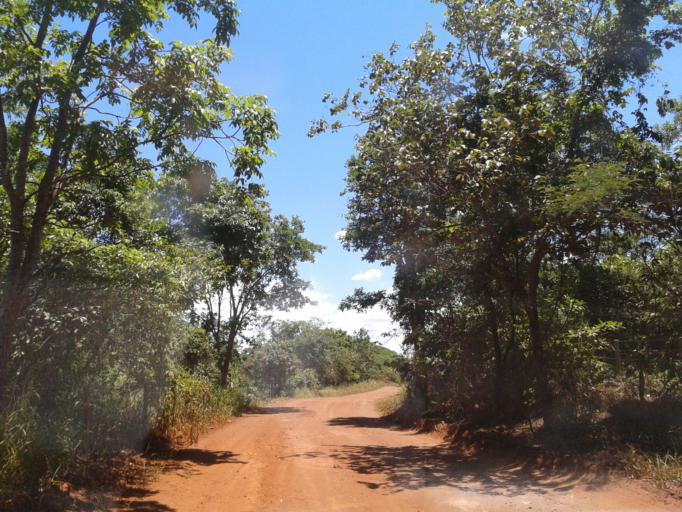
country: BR
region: Minas Gerais
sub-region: Centralina
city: Centralina
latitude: -18.6876
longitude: -49.2210
